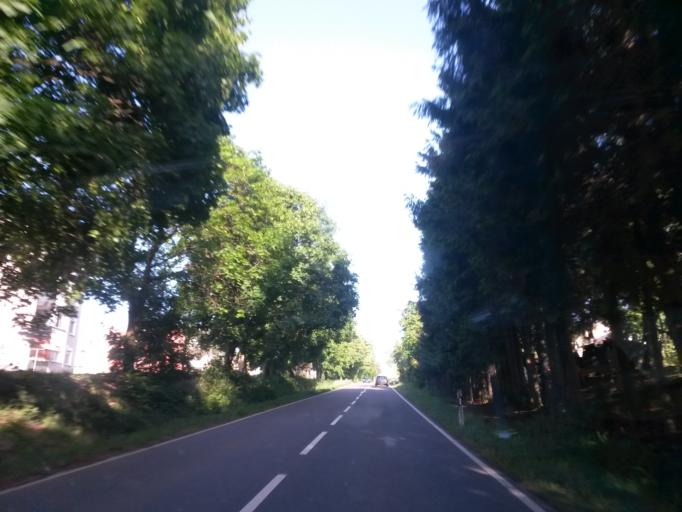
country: DE
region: North Rhine-Westphalia
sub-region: Regierungsbezirk Koln
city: Much
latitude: 50.9398
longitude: 7.4632
